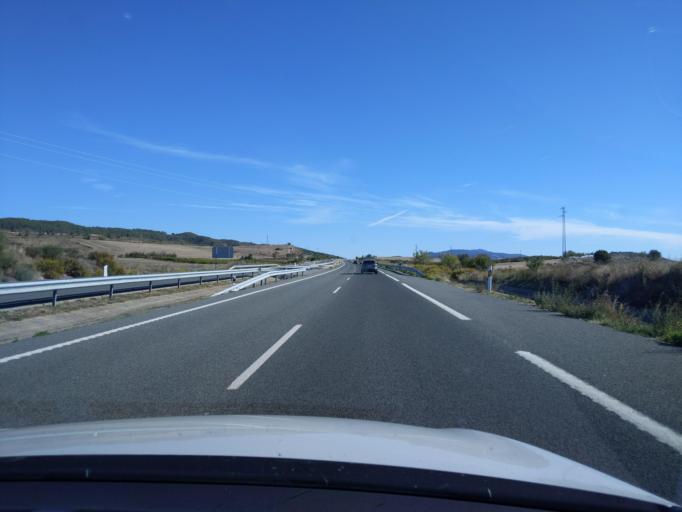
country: ES
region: Navarre
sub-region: Provincia de Navarra
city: Los Arcos
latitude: 42.5730
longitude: -2.1594
